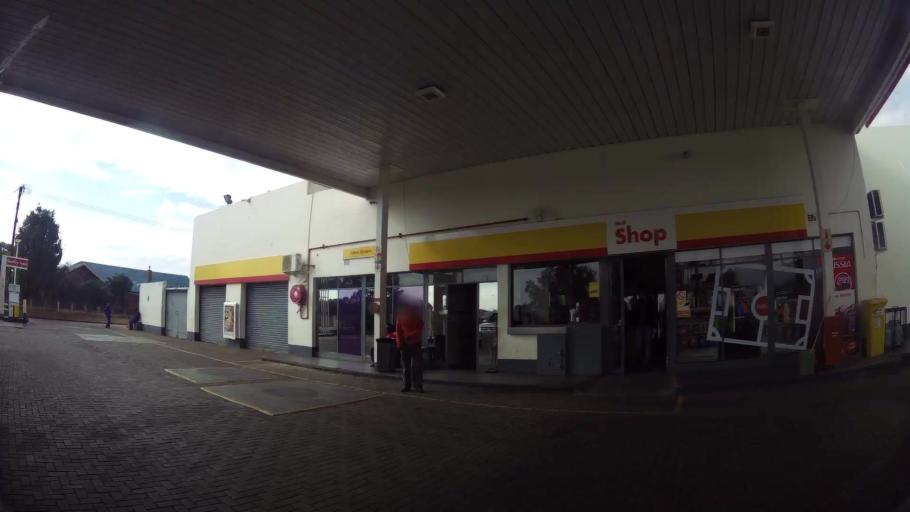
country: ZA
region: Gauteng
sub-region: Sedibeng District Municipality
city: Meyerton
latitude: -26.5957
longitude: 27.9921
